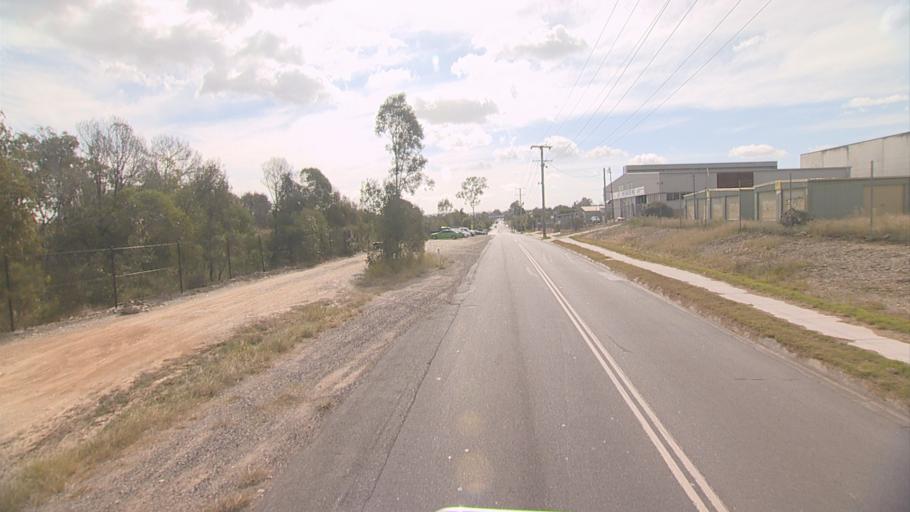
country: AU
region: Queensland
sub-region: Logan
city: Waterford West
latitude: -27.7039
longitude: 153.1545
